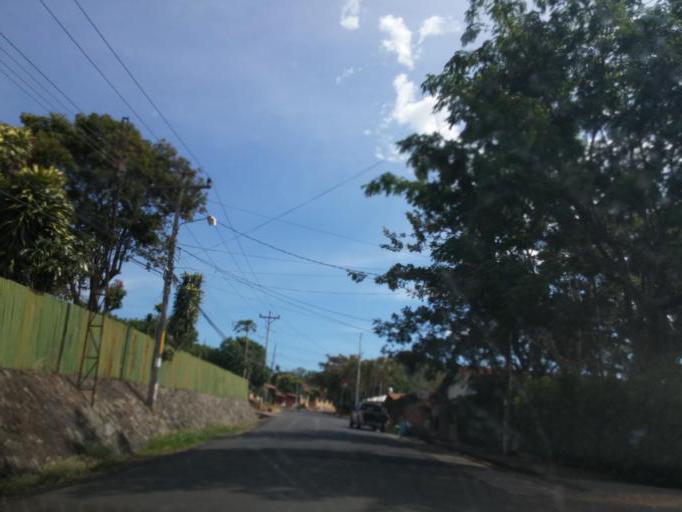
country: CR
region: Alajuela
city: Alajuela
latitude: 10.0406
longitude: -84.2204
